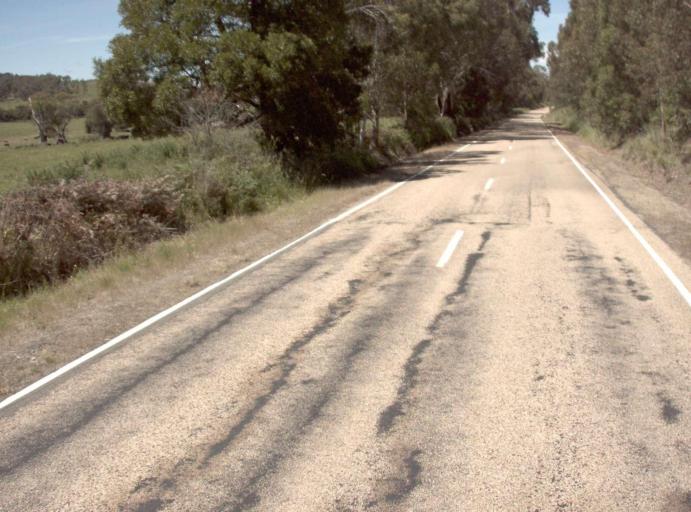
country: AU
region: Victoria
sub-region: East Gippsland
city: Lakes Entrance
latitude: -37.1788
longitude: 148.2690
